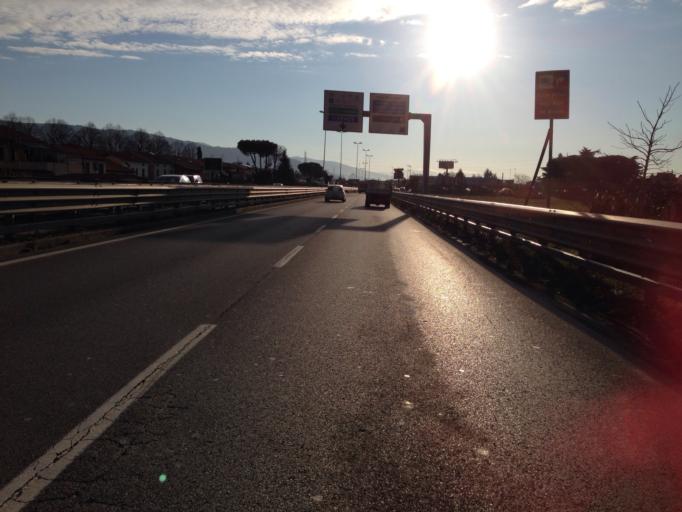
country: IT
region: Tuscany
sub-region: Provincia di Prato
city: Prato
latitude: 43.8798
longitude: 11.0590
